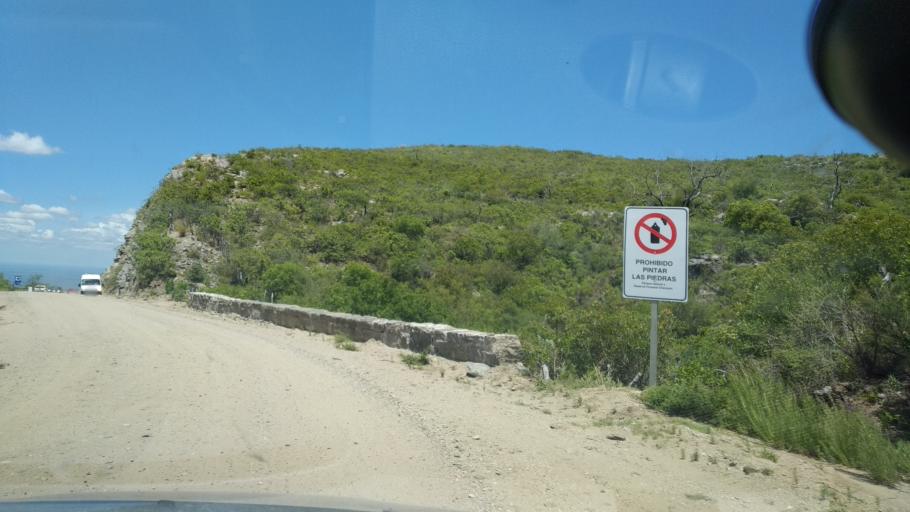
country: AR
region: Cordoba
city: Salsacate
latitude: -31.3776
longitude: -65.3970
